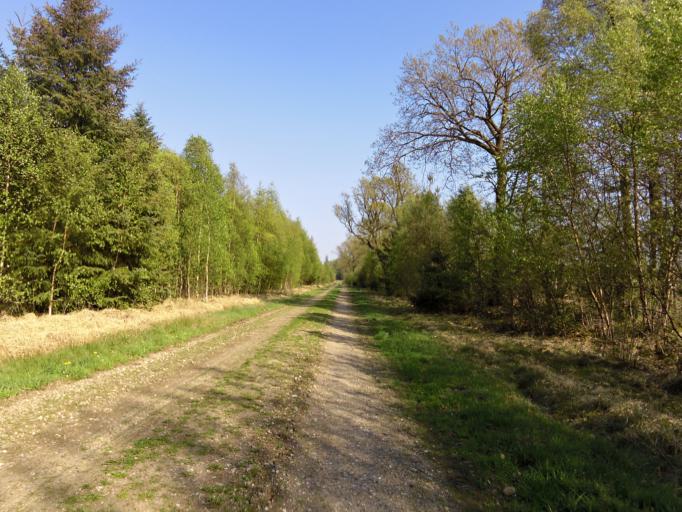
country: DK
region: South Denmark
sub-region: Tonder Kommune
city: Toftlund
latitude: 55.1954
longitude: 8.9423
